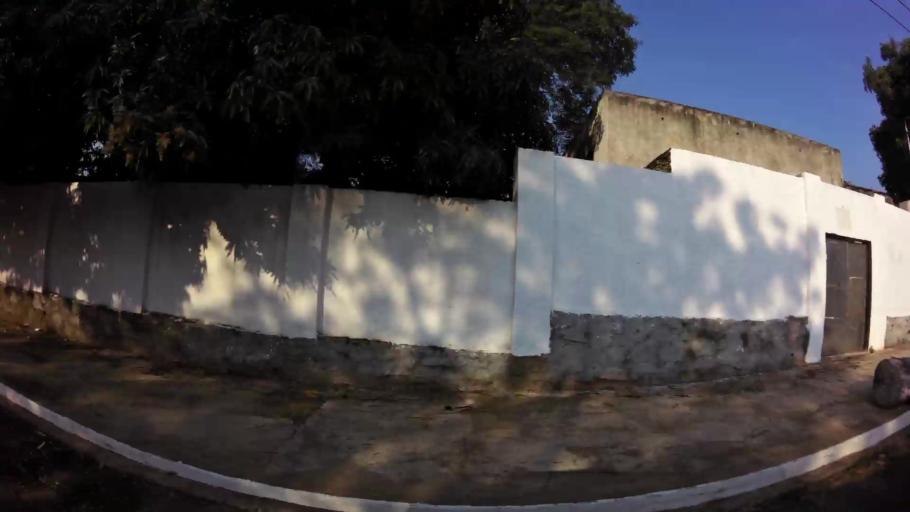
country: PY
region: Central
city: Lambare
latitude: -25.3421
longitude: -57.5977
